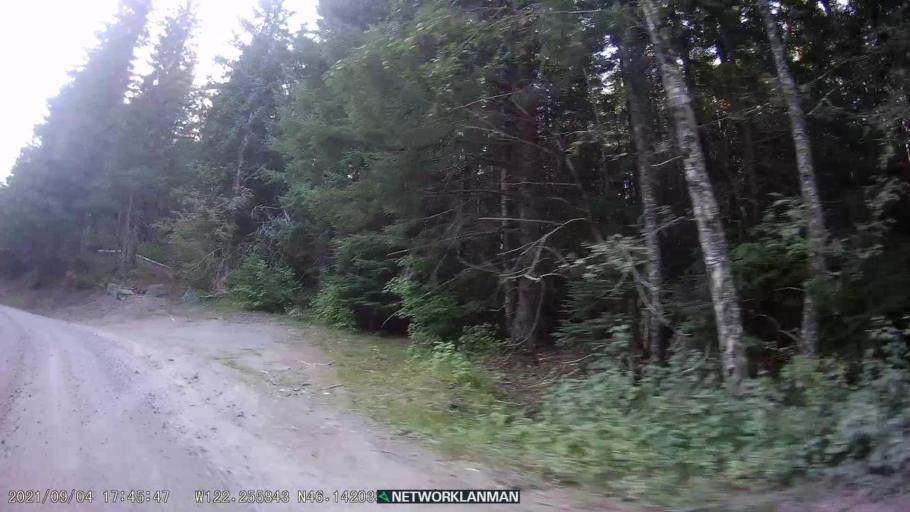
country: US
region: Washington
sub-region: Clark County
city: Amboy
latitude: 46.1421
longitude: -122.2558
